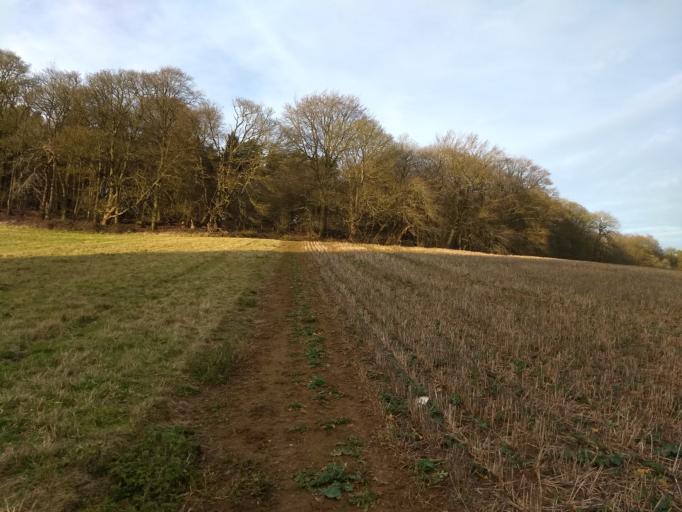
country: GB
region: England
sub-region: Central Bedfordshire
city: Woburn
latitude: 51.9929
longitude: -0.6378
